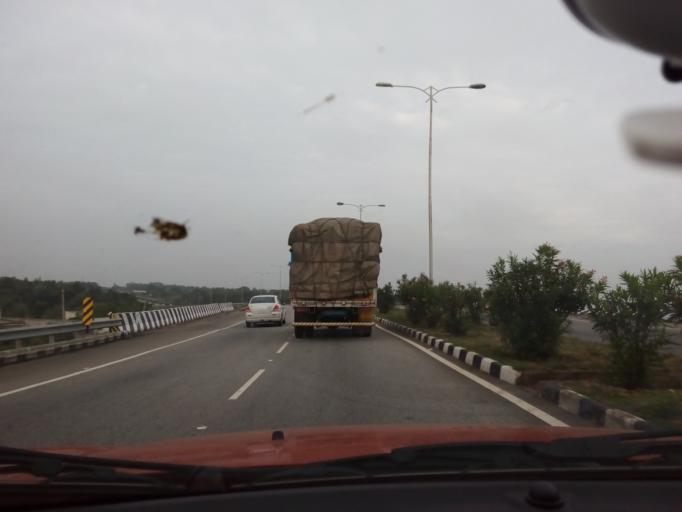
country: IN
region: Karnataka
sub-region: Tumkur
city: Kunigal
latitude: 13.0032
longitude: 76.9558
